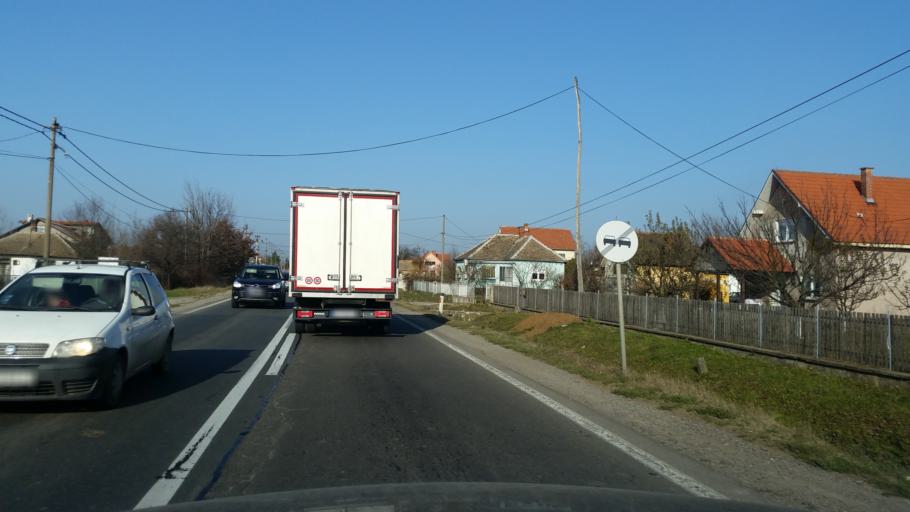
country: RS
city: Stepojevac
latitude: 44.5221
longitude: 20.2933
